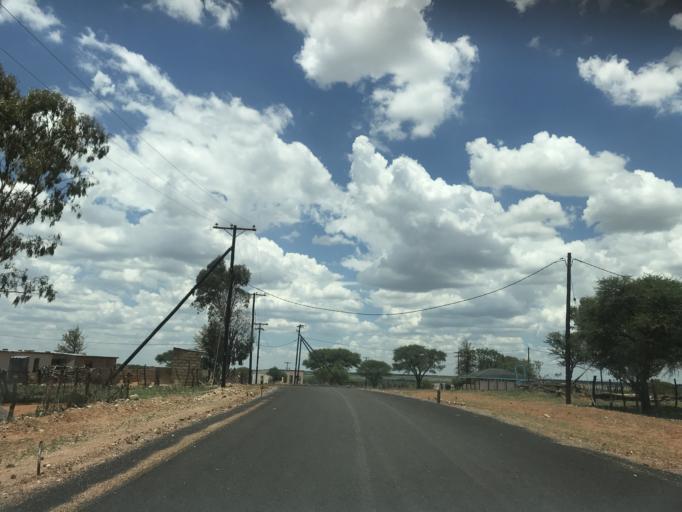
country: BW
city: Mabuli
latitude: -25.7905
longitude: 24.9010
